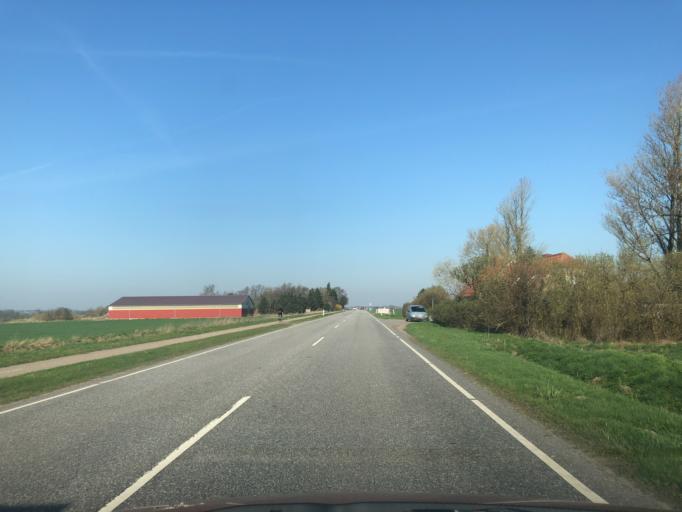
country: DK
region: Zealand
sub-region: Faxe Kommune
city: Haslev
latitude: 55.3646
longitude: 11.8773
